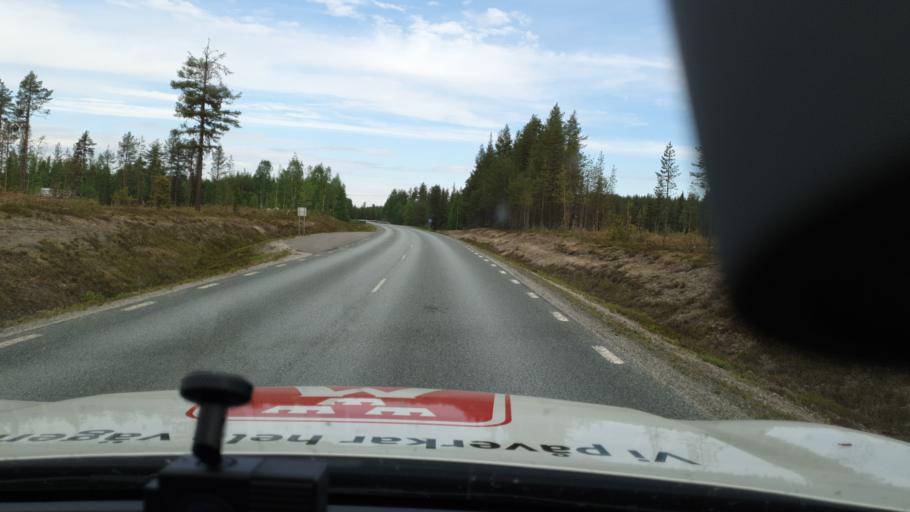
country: SE
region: Vaesterbotten
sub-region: Mala Kommun
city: Mala
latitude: 65.0537
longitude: 18.3895
